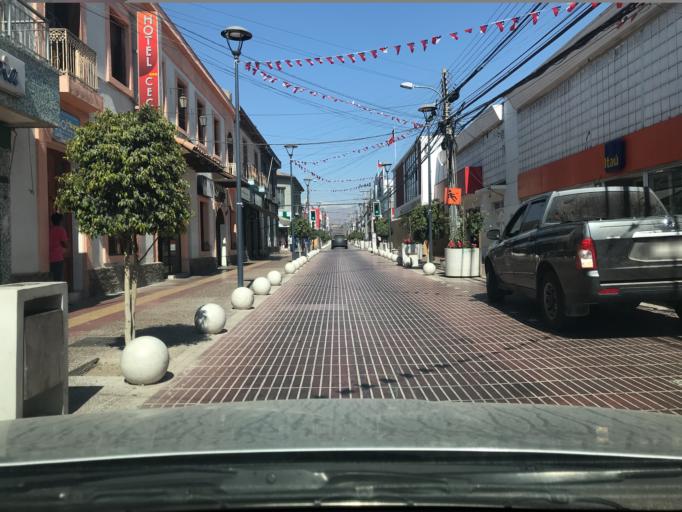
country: CL
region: Atacama
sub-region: Provincia de Huasco
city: Vallenar
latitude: -28.5766
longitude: -70.7590
